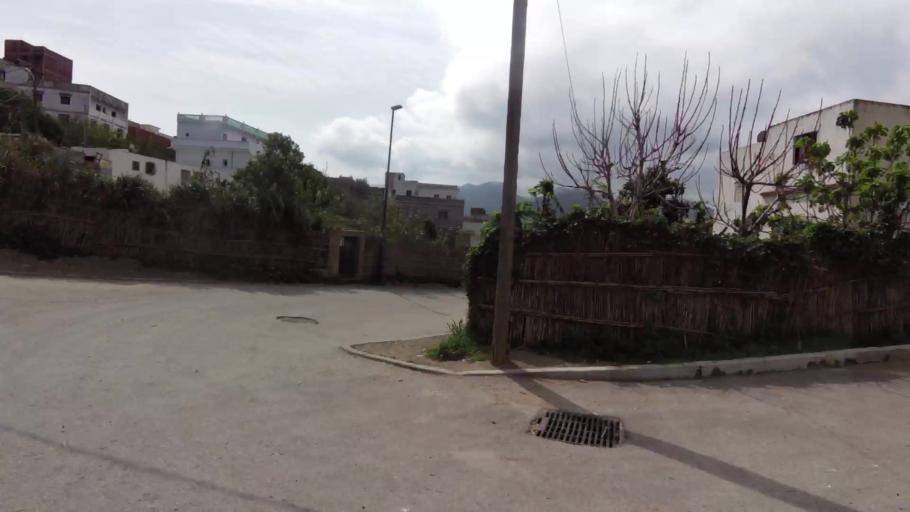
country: MA
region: Tanger-Tetouan
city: Tetouan
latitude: 35.5801
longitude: -5.3978
